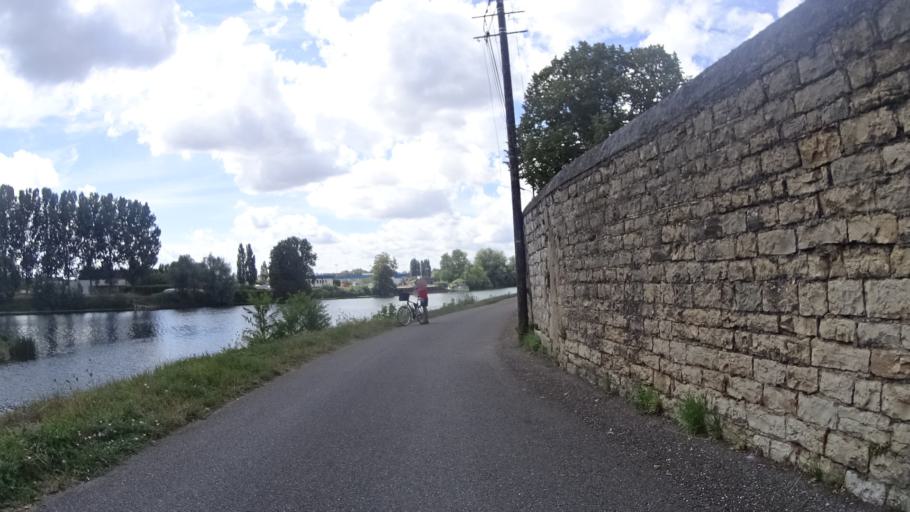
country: FR
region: Franche-Comte
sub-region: Departement du Jura
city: Dole
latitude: 47.0880
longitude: 5.4916
